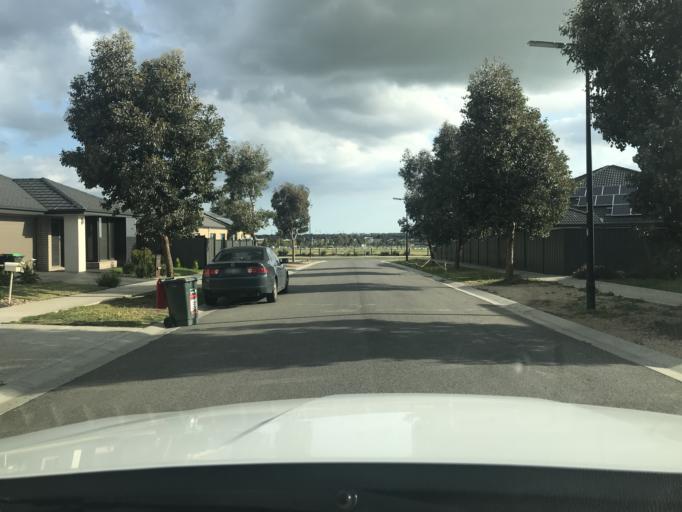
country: AU
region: Victoria
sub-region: Hume
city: Craigieburn
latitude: -37.5801
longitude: 144.9034
